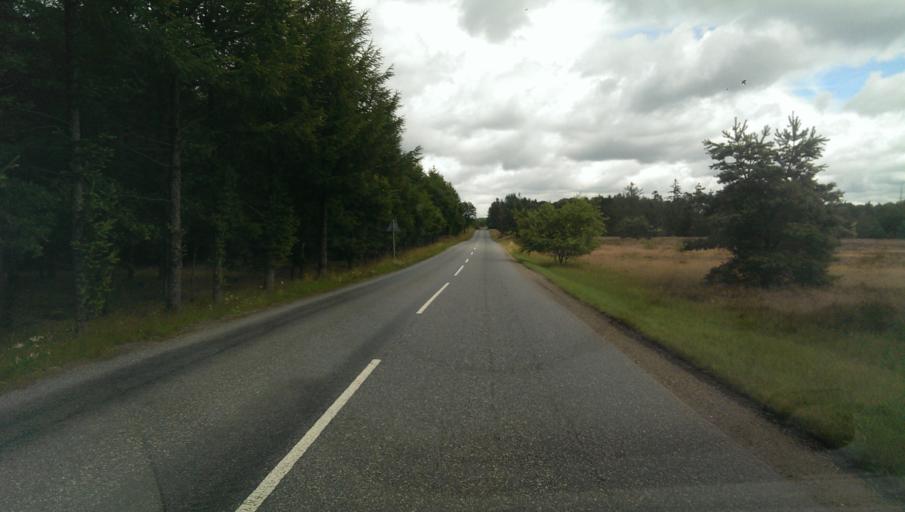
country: DK
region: Central Jutland
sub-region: Silkeborg Kommune
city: Virklund
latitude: 56.0877
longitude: 9.4293
